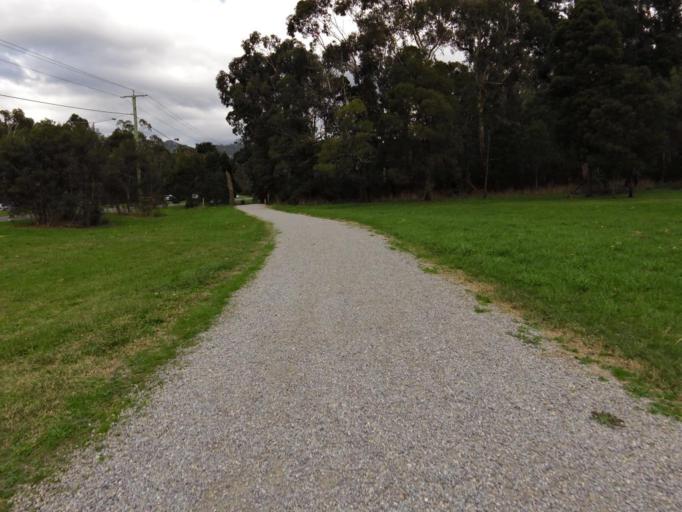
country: AU
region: Victoria
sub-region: Yarra Ranges
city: Mount Evelyn
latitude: -37.7870
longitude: 145.3612
